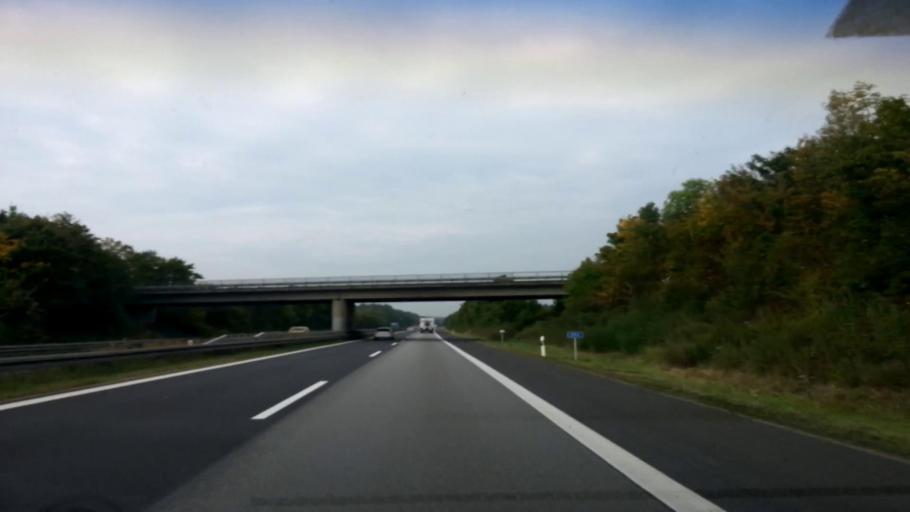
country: DE
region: Bavaria
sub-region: Regierungsbezirk Unterfranken
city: Wonfurt
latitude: 50.0049
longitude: 10.4649
